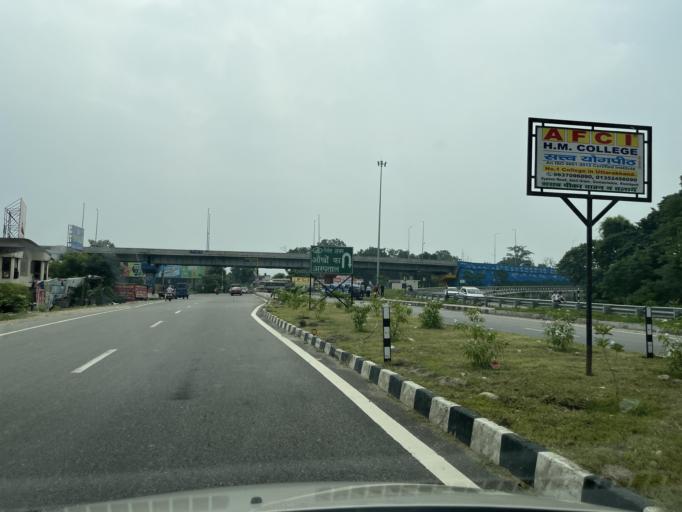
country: IN
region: Uttarakhand
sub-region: Dehradun
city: Raiwala
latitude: 30.0552
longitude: 78.2191
